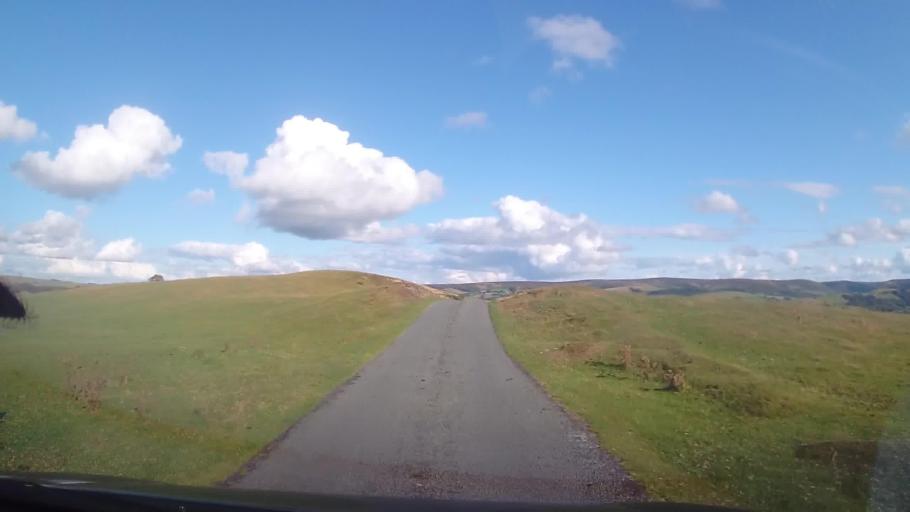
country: GB
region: England
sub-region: Shropshire
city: Norbury
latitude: 52.5729
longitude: -2.9232
